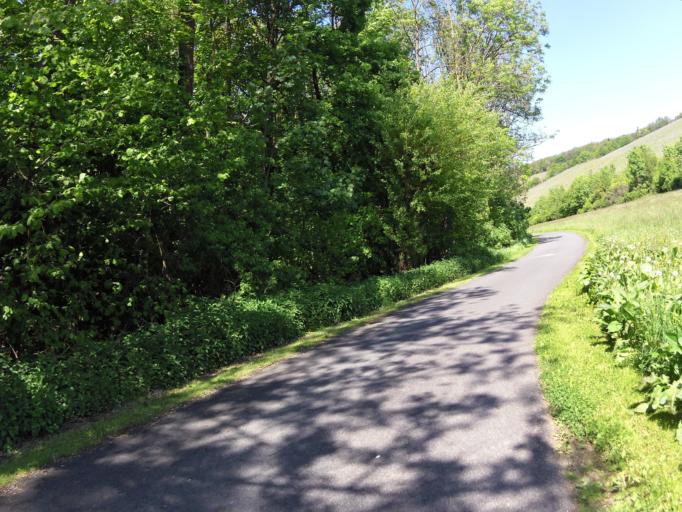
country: DE
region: Bavaria
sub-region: Regierungsbezirk Unterfranken
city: Eibelstadt
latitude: 49.7326
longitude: 10.0146
